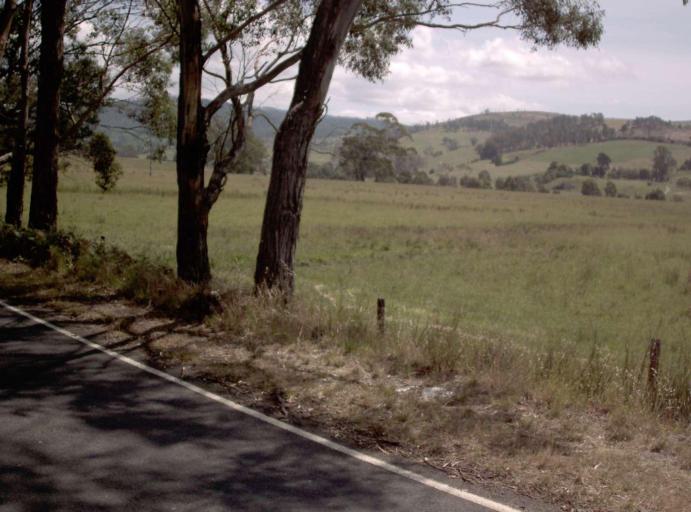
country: AU
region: Victoria
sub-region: Latrobe
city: Traralgon
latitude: -38.2977
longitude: 146.5380
